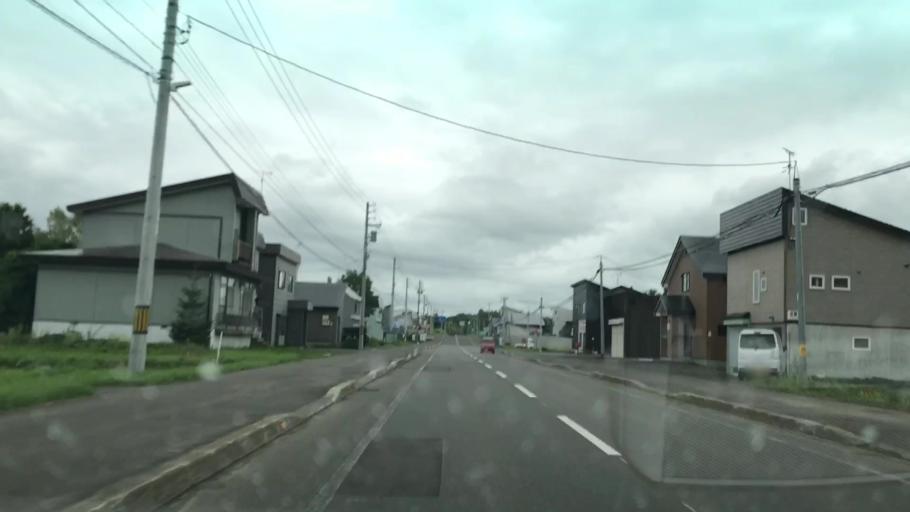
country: JP
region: Hokkaido
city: Niseko Town
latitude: 42.7972
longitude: 140.7087
